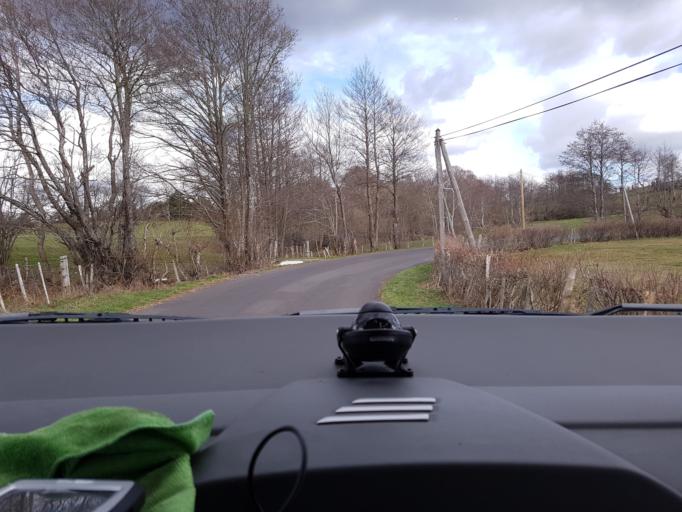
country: FR
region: Midi-Pyrenees
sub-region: Departement de l'Aveyron
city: Laguiole
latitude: 44.7021
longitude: 2.8424
